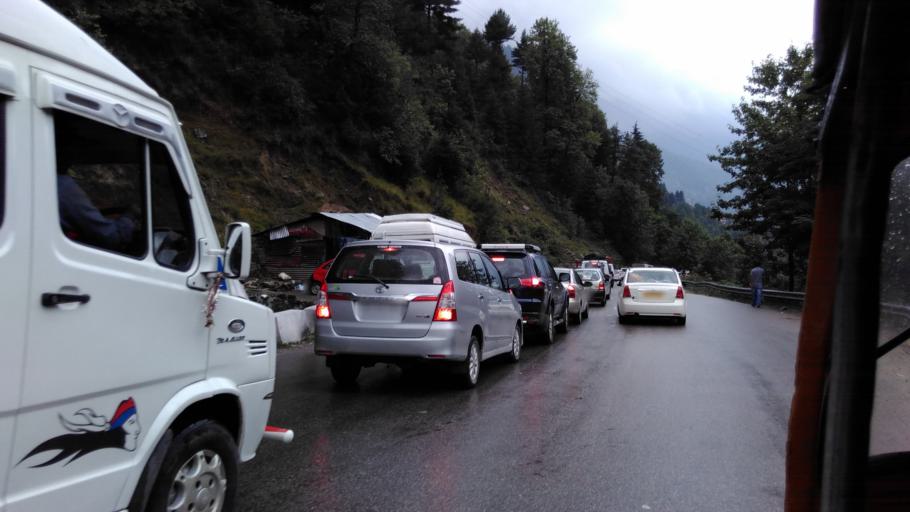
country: IN
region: Himachal Pradesh
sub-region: Kulu
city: Manali
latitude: 32.2531
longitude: 77.1891
